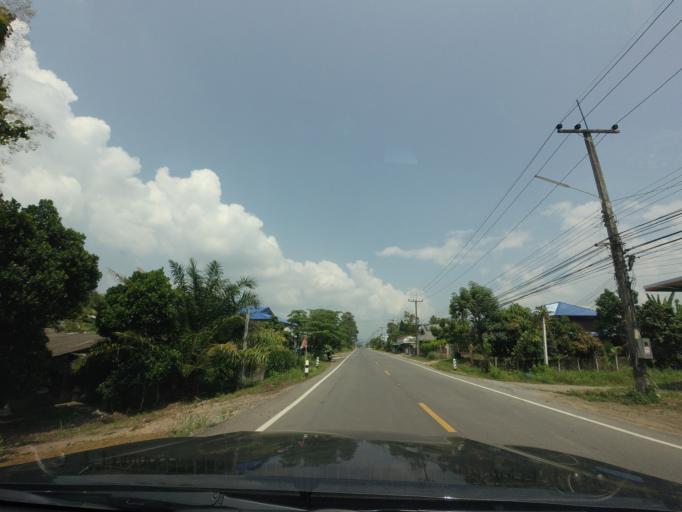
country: TH
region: Nan
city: Santi Suk
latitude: 18.9410
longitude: 100.9243
